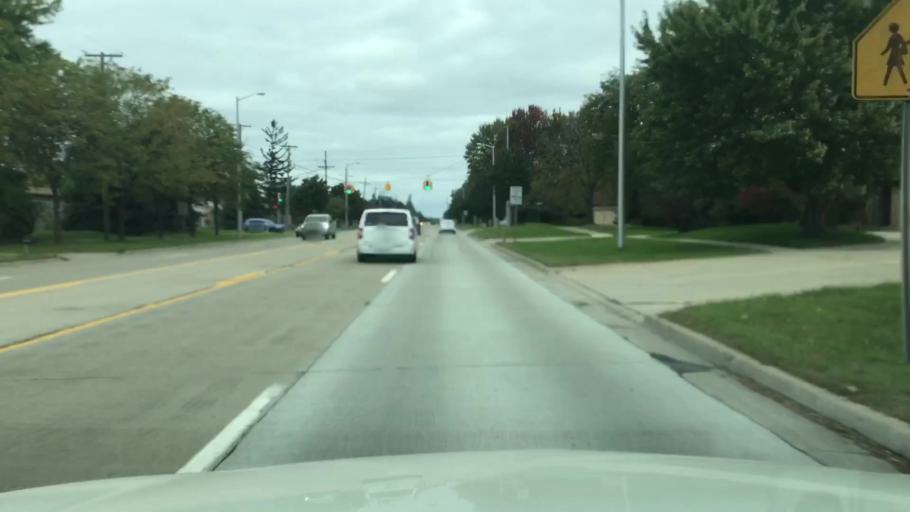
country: US
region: Michigan
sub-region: Macomb County
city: Sterling Heights
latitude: 42.5840
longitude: -83.0704
